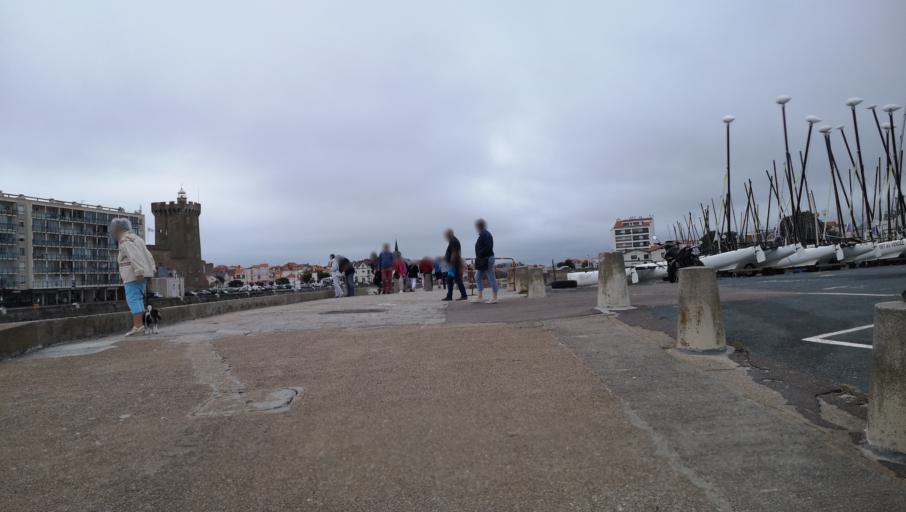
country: FR
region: Pays de la Loire
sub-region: Departement de la Vendee
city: Les Sables-d'Olonne
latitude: 46.4925
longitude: -1.7935
